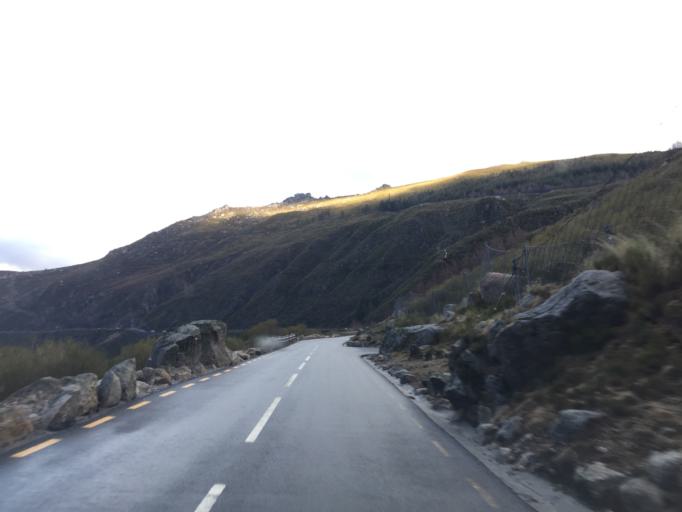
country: PT
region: Guarda
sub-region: Manteigas
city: Manteigas
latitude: 40.3263
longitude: -7.5815
